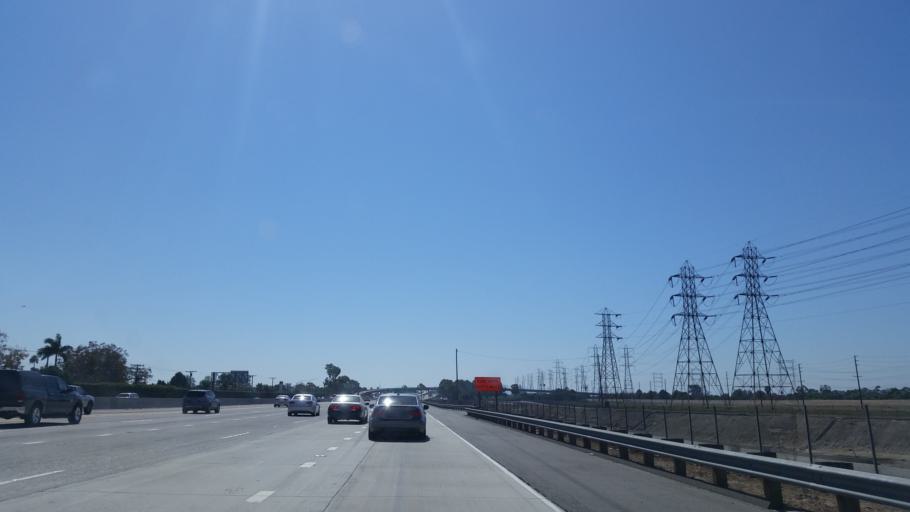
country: US
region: California
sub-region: Orange County
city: Rossmoor
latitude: 33.7954
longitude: -118.0871
